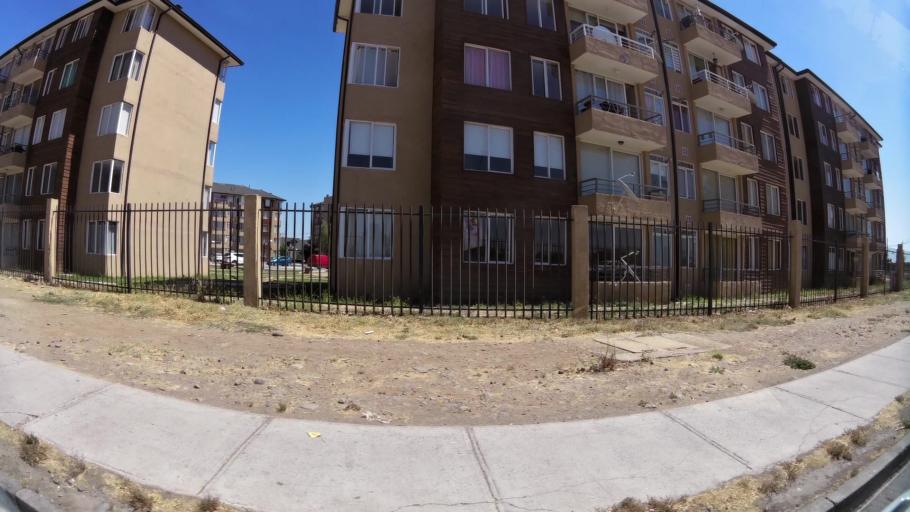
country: CL
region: Maule
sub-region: Provincia de Curico
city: Curico
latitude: -34.9726
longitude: -71.2191
